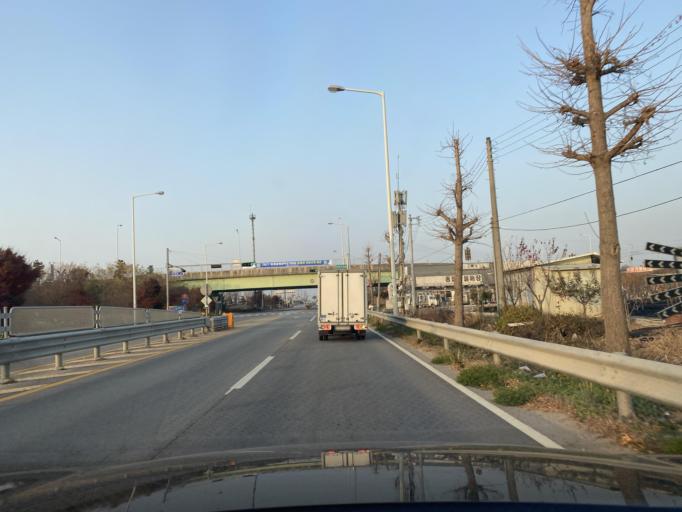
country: KR
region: Chungcheongnam-do
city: Yesan
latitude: 36.7029
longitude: 126.8301
